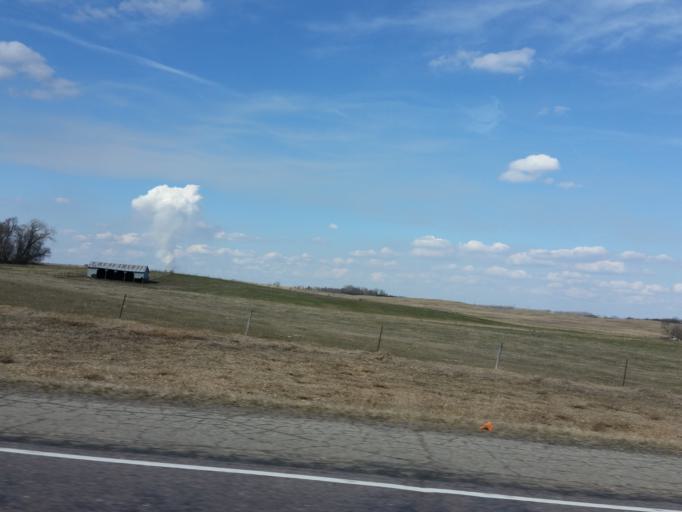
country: US
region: Minnesota
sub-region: Lac qui Parle County
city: Madison
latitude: 44.9357
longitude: -96.3569
